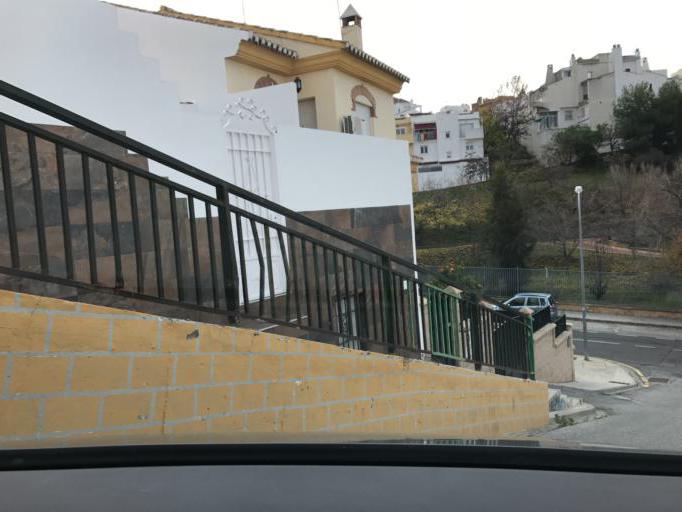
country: ES
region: Andalusia
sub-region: Provincia de Granada
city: Huetor Vega
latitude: 37.1502
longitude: -3.5685
